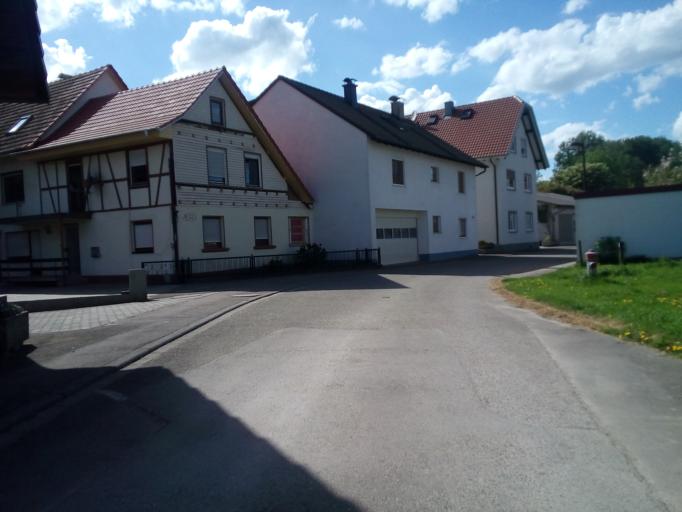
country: DE
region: Baden-Wuerttemberg
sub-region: Karlsruhe Region
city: Lichtenau
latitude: 48.7037
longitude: 8.0000
